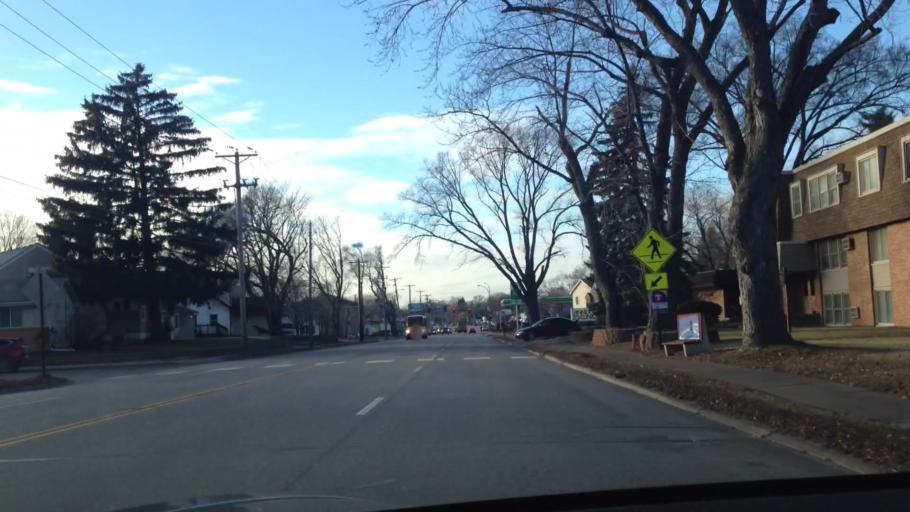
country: US
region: Minnesota
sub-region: Hennepin County
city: Crystal
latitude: 45.0318
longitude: -93.3532
